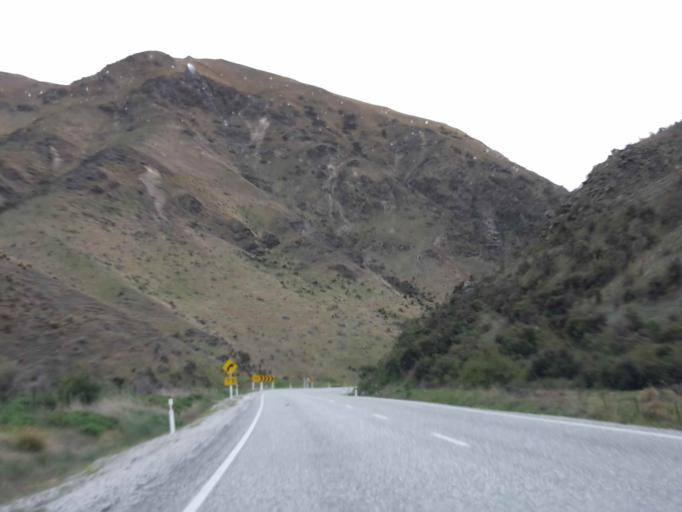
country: NZ
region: Otago
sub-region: Queenstown-Lakes District
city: Wanaka
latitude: -44.6008
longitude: 169.5530
